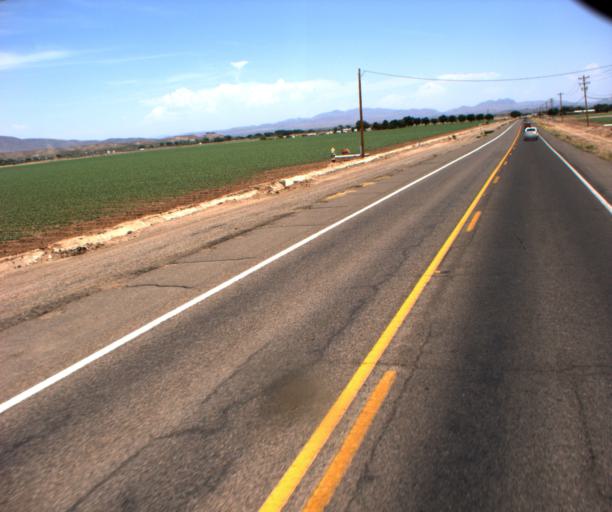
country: US
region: Arizona
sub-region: Graham County
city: Safford
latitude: 32.8166
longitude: -109.6472
